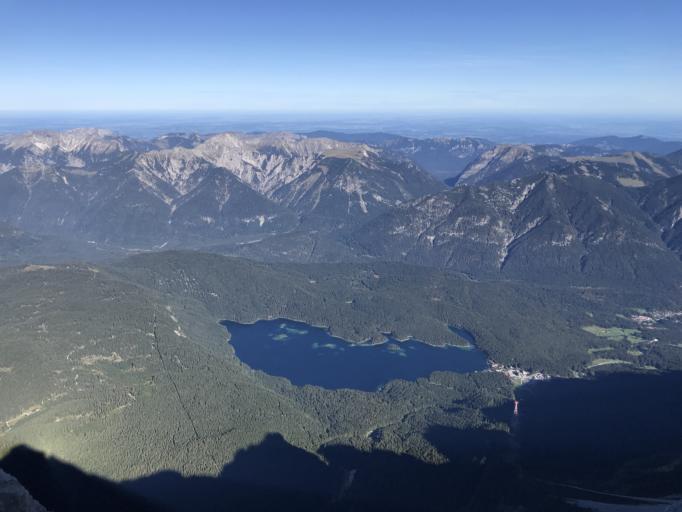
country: DE
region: Bavaria
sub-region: Upper Bavaria
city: Grainau
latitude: 47.4215
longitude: 10.9857
